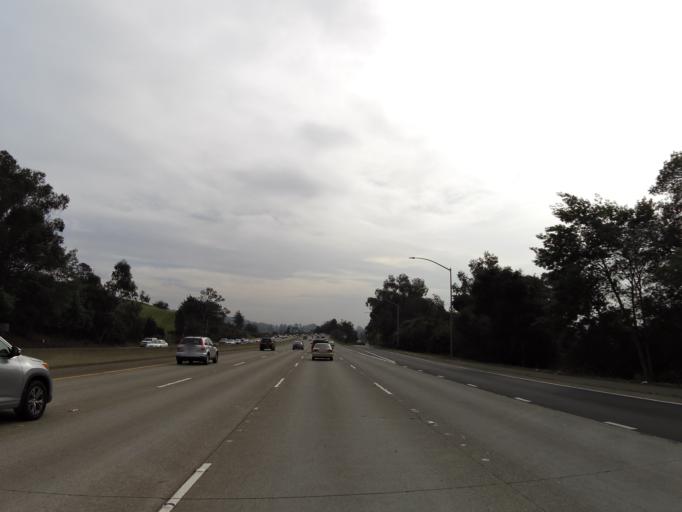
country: US
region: California
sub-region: Alameda County
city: San Leandro
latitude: 37.7495
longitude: -122.1513
